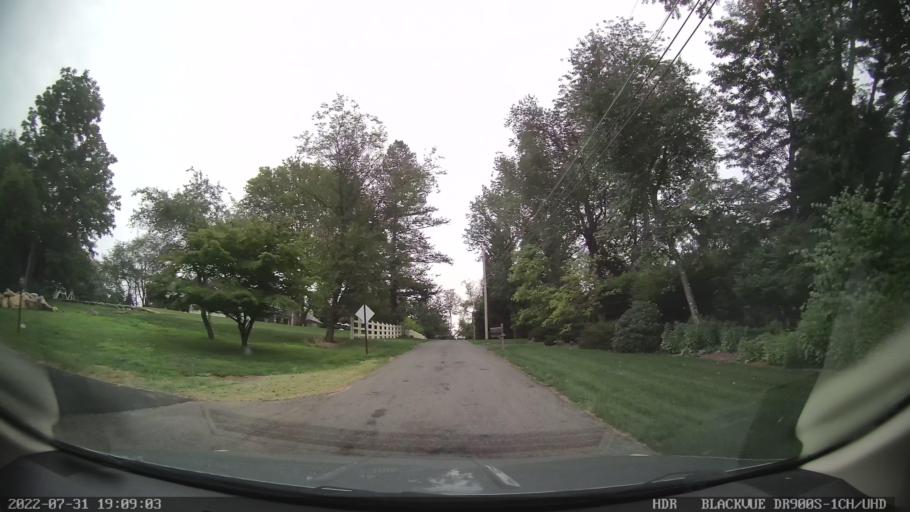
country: US
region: Pennsylvania
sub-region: Northampton County
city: Hellertown
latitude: 40.5736
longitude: -75.3654
